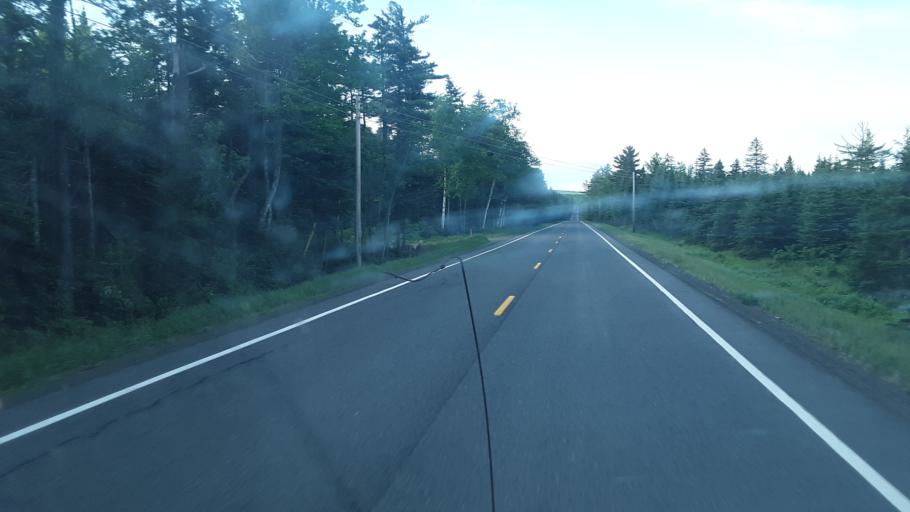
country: US
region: Maine
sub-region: Penobscot County
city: Patten
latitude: 46.2484
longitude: -68.3403
